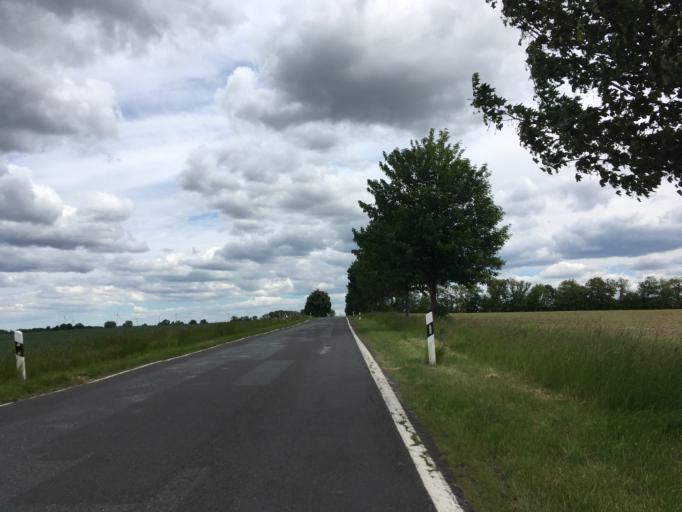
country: DE
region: Brandenburg
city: Werftpfuhl
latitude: 52.7350
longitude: 13.8172
